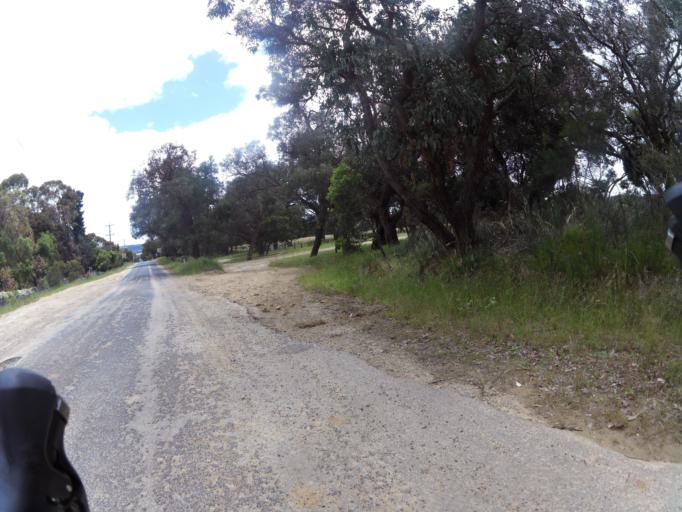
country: AU
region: Victoria
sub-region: Mornington Peninsula
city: Safety Beach
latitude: -38.3452
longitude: 145.0132
